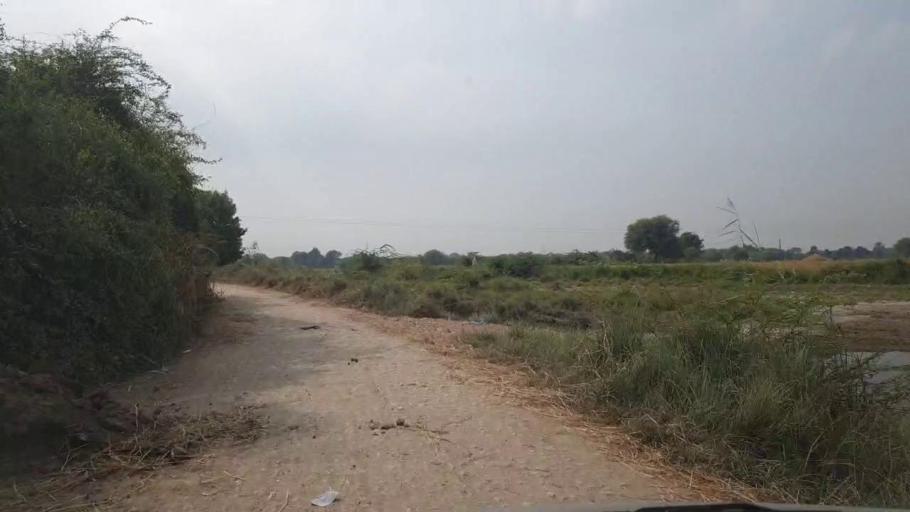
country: PK
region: Sindh
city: Talhar
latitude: 24.8863
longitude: 68.8016
